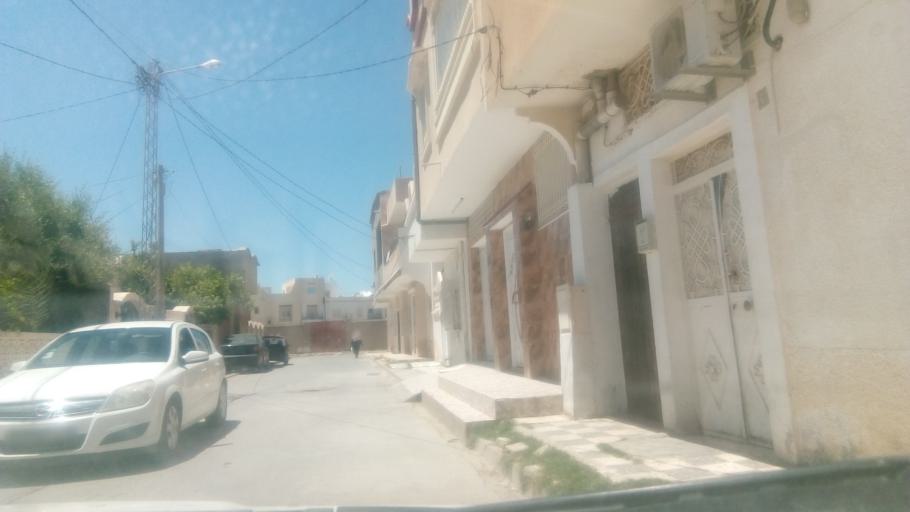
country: TN
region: Al Qayrawan
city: Kairouan
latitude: 35.6679
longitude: 10.0863
